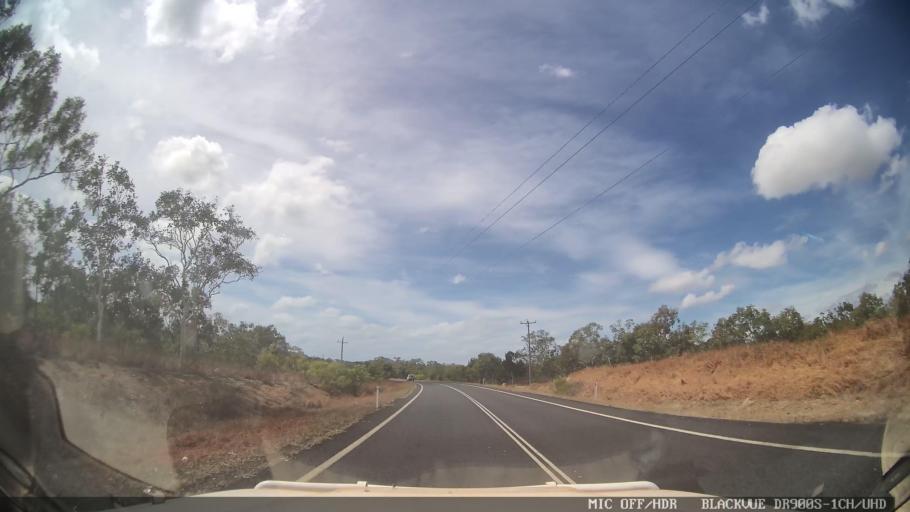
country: AU
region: Queensland
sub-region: Cook
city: Cooktown
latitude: -15.5350
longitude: 145.2330
